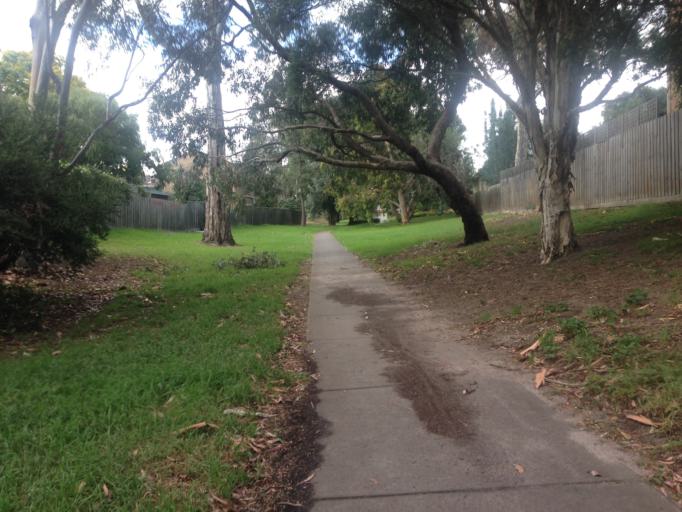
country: AU
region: Victoria
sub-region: Boroondara
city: Balwyn North
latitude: -37.7828
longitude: 145.0858
